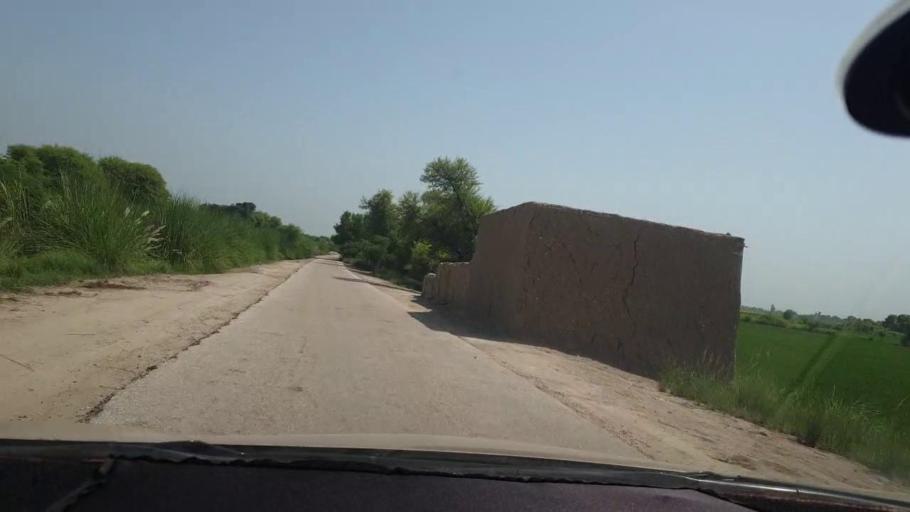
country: PK
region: Sindh
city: Kambar
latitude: 27.5210
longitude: 68.0084
